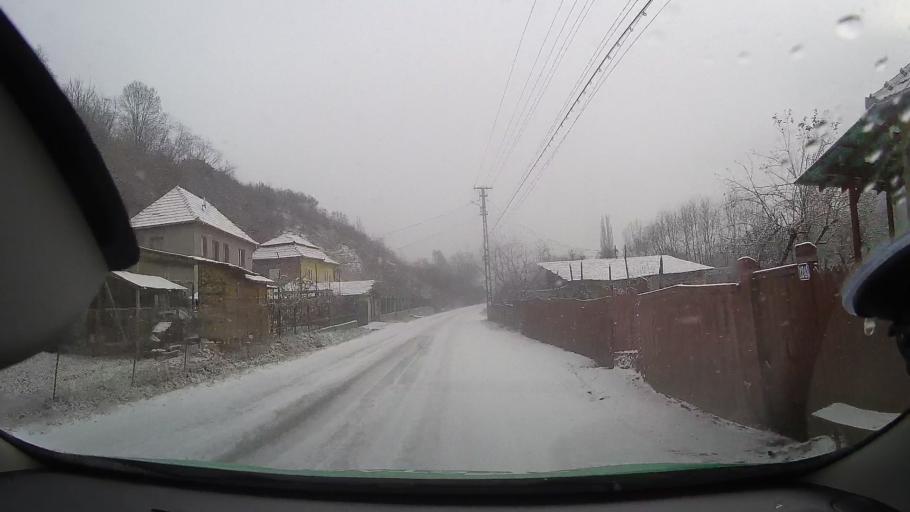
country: RO
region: Alba
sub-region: Comuna Livezile
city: Livezile
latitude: 46.3509
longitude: 23.6243
